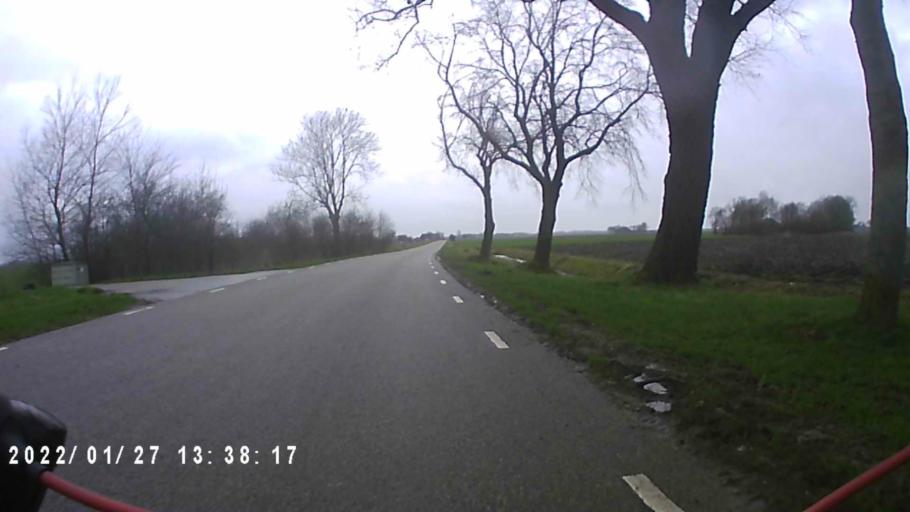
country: NL
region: Friesland
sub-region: Gemeente Kollumerland en Nieuwkruisland
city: Kollum
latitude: 53.2964
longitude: 6.2234
